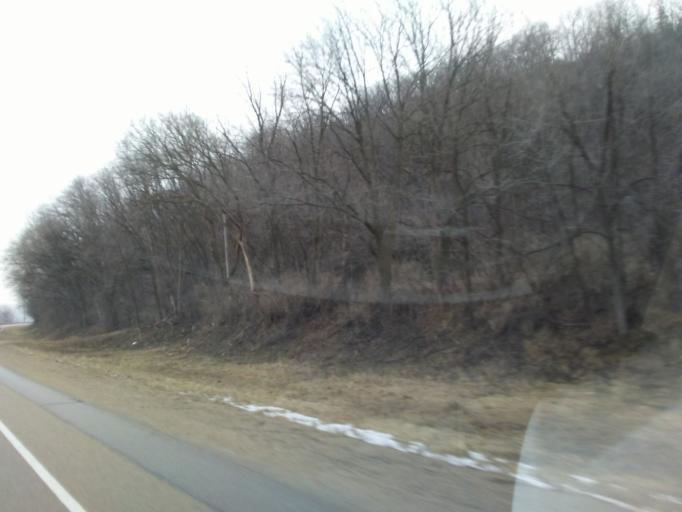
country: US
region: Wisconsin
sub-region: Dane County
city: Black Earth
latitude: 43.1443
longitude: -89.7536
